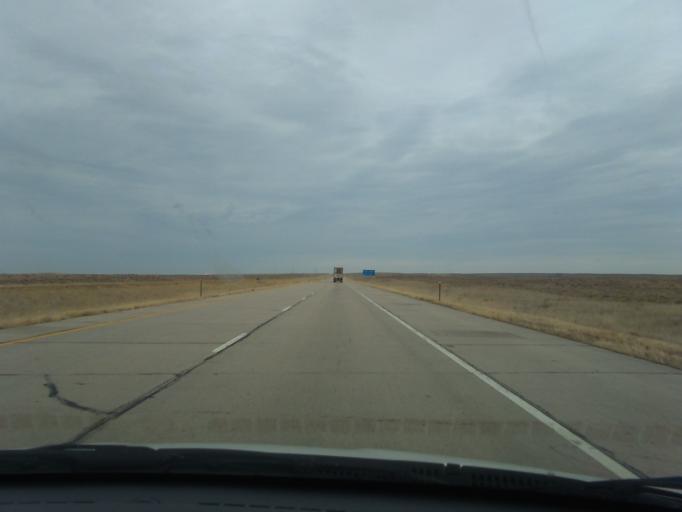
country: US
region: Colorado
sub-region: Weld County
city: Keenesburg
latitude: 40.2079
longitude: -104.2376
